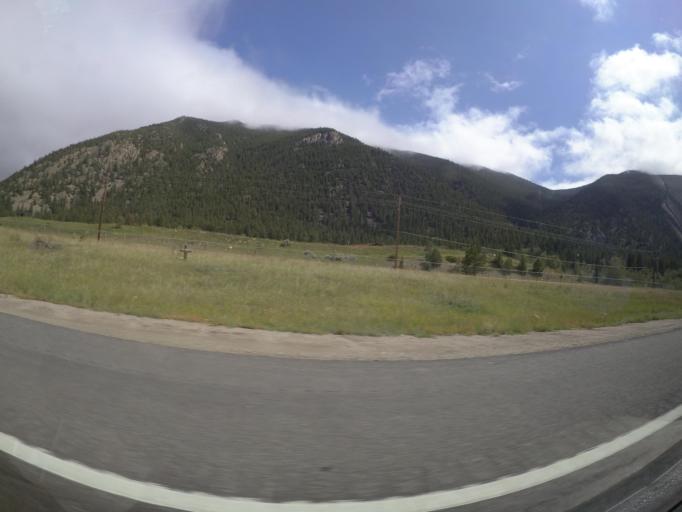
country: US
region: Colorado
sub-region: Clear Creek County
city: Georgetown
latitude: 39.7530
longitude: -105.6623
